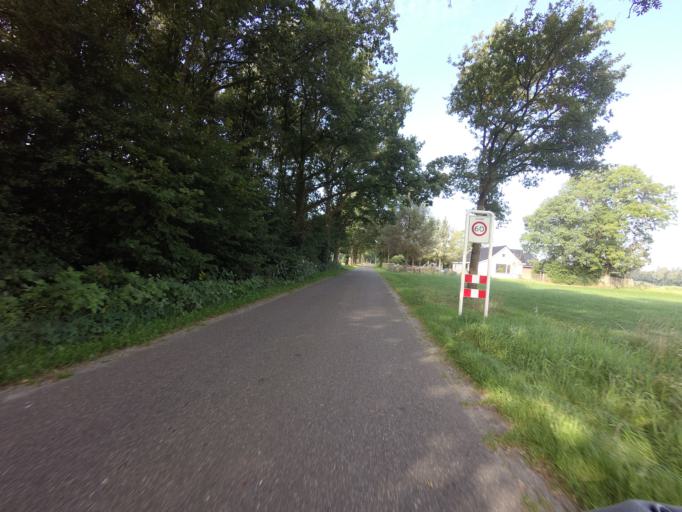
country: NL
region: Friesland
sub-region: Gemeente Weststellingwerf
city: Noordwolde
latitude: 52.9141
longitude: 6.1491
